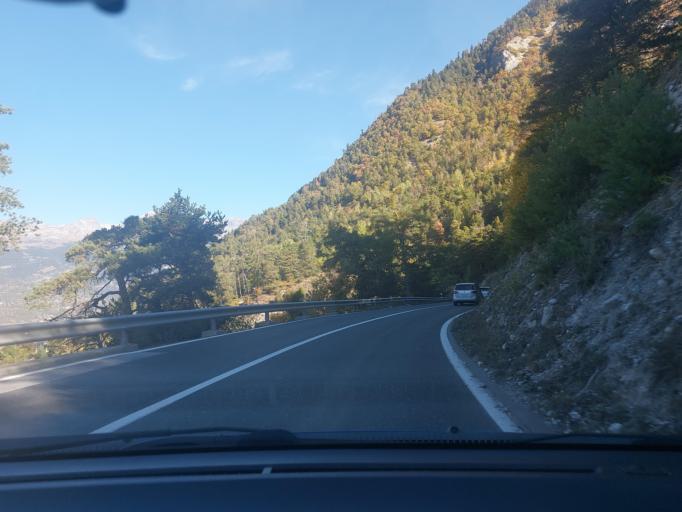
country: CH
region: Valais
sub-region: Sierre District
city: Chippis
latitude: 46.2660
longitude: 7.5559
